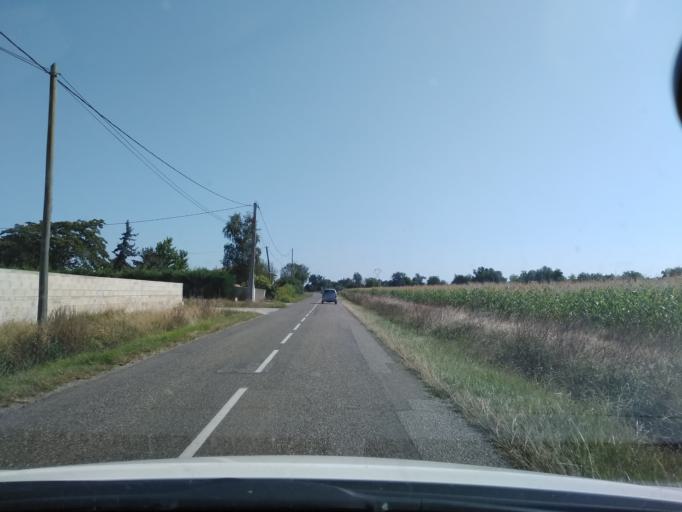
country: FR
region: Midi-Pyrenees
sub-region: Departement du Tarn-et-Garonne
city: Montech
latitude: 43.9764
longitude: 1.2456
